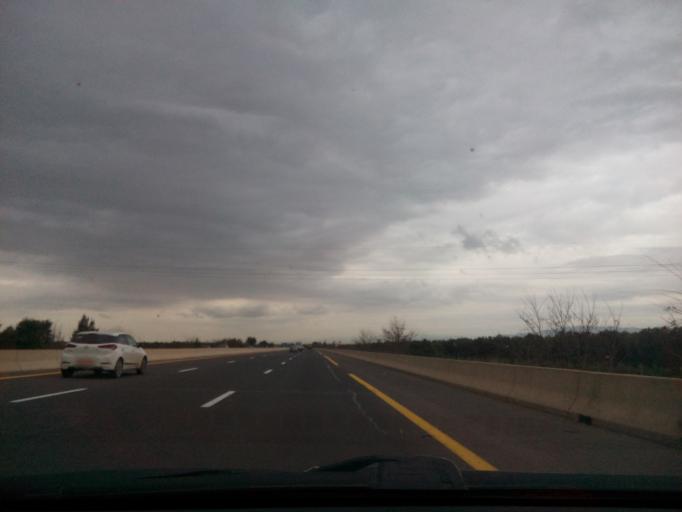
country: DZ
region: Mascara
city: Sig
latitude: 35.5812
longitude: -0.2341
